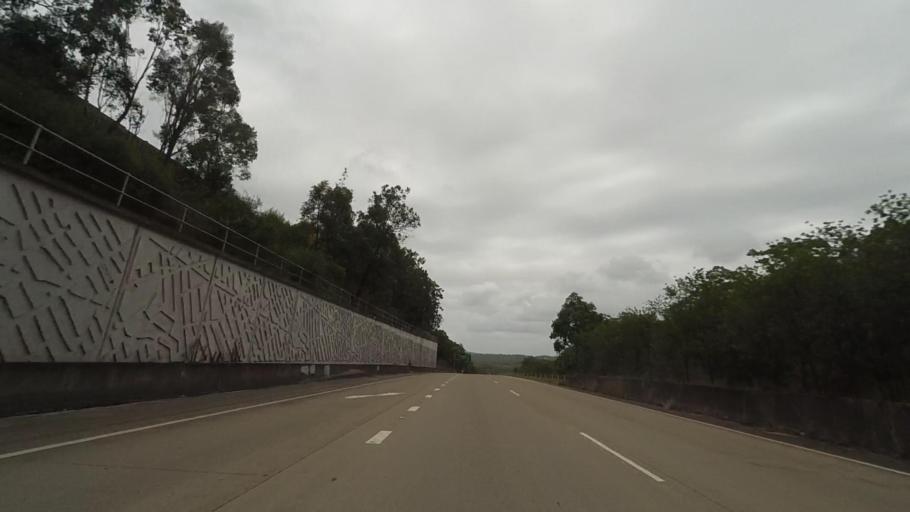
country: AU
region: New South Wales
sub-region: Lake Macquarie Shire
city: Kotara
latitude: -32.9508
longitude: 151.6837
